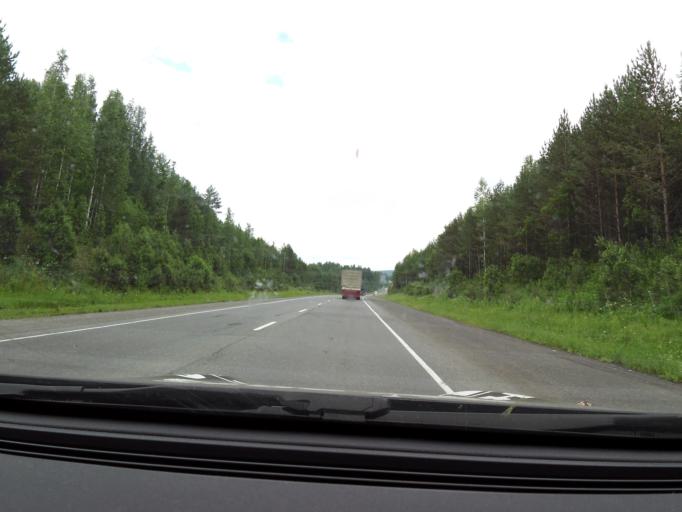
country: RU
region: Sverdlovsk
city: Druzhinino
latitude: 56.8351
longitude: 59.6396
